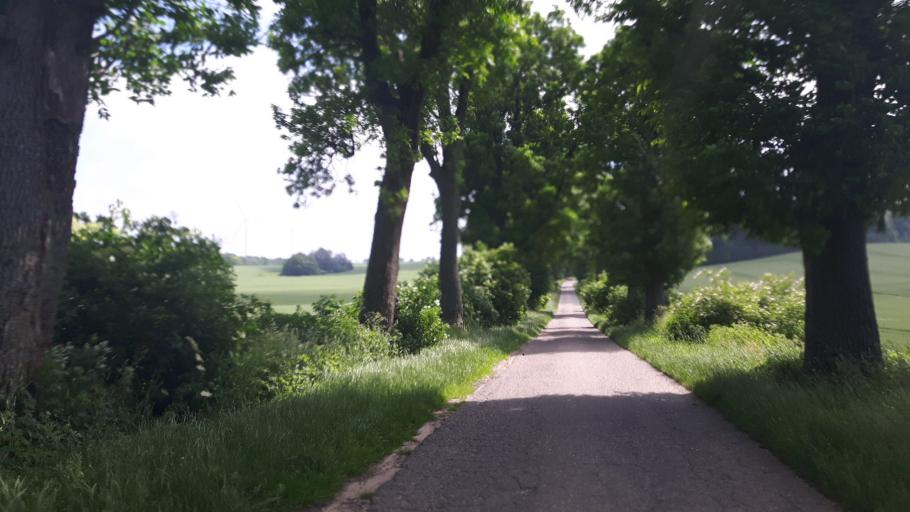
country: PL
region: West Pomeranian Voivodeship
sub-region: Powiat slawienski
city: Darlowo
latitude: 54.4691
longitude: 16.4856
